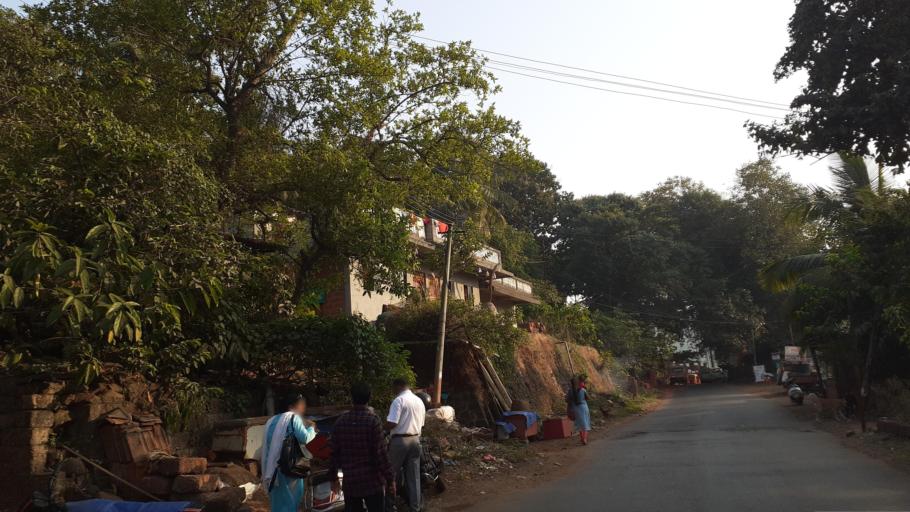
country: IN
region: Maharashtra
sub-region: Ratnagiri
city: Ratnagiri
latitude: 17.0434
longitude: 73.2978
